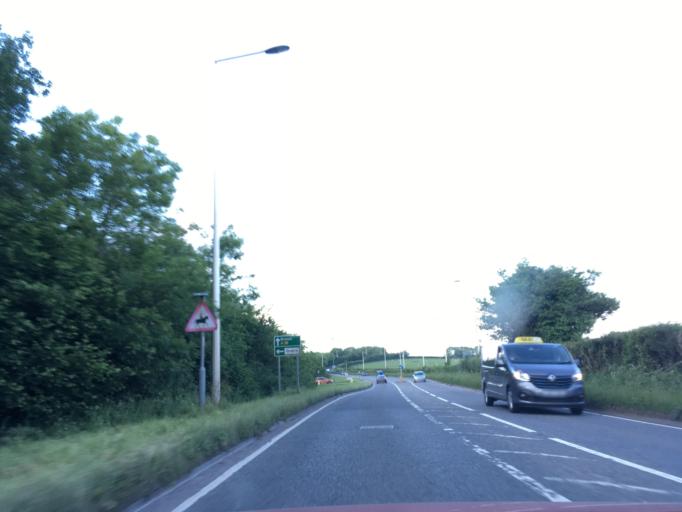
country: GB
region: England
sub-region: North Somerset
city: Winford
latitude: 51.3930
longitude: -2.6958
